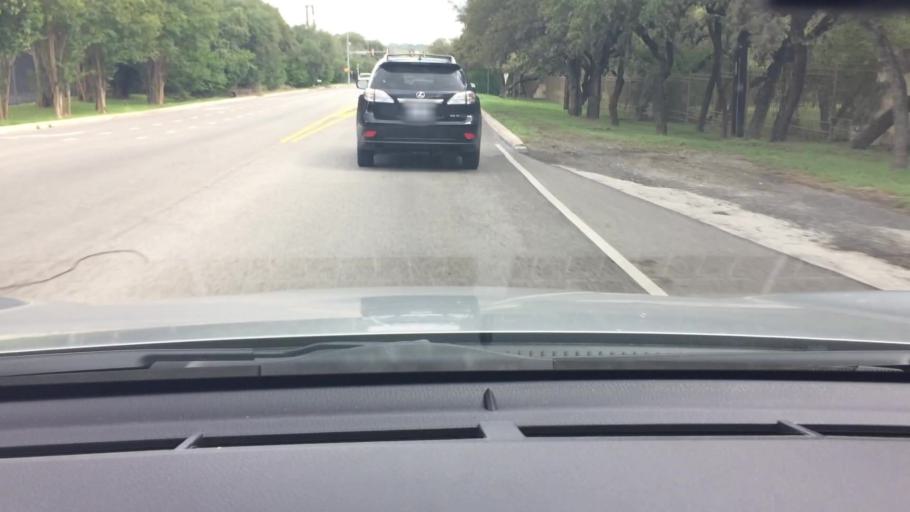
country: US
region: Texas
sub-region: Bexar County
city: Shavano Park
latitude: 29.5576
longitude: -98.5494
